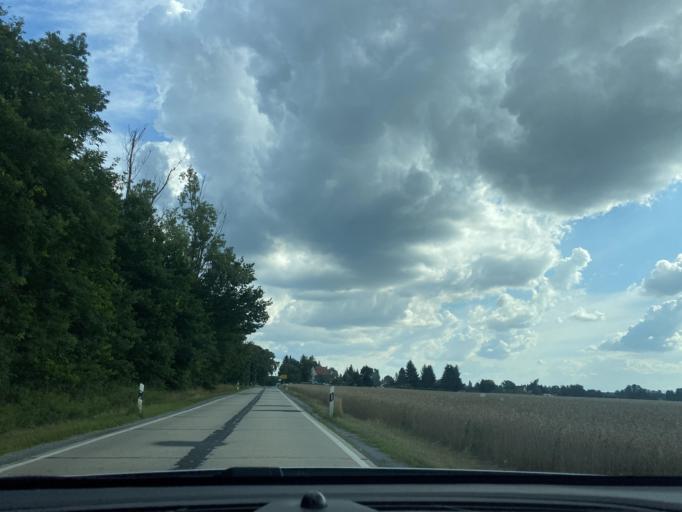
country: DE
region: Saxony
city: Klitten
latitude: 51.3561
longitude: 14.6075
